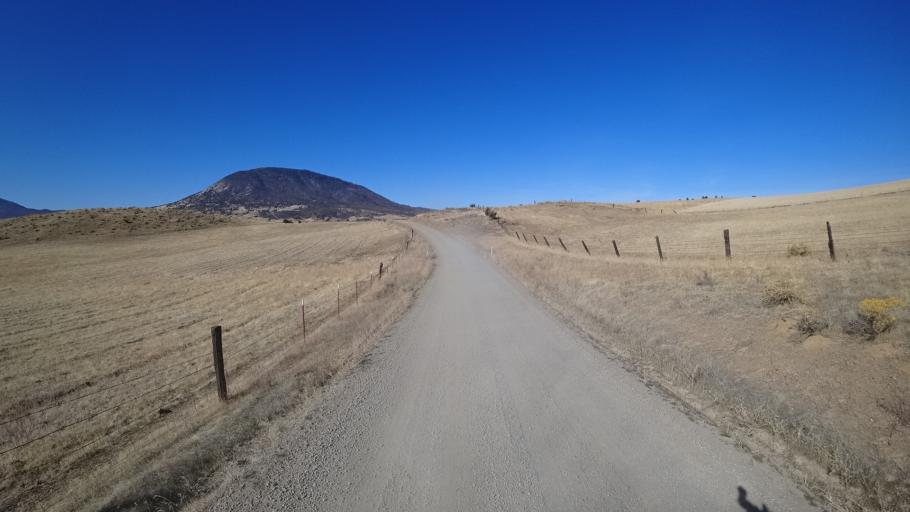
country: US
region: California
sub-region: Siskiyou County
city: Montague
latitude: 41.8470
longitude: -122.4469
